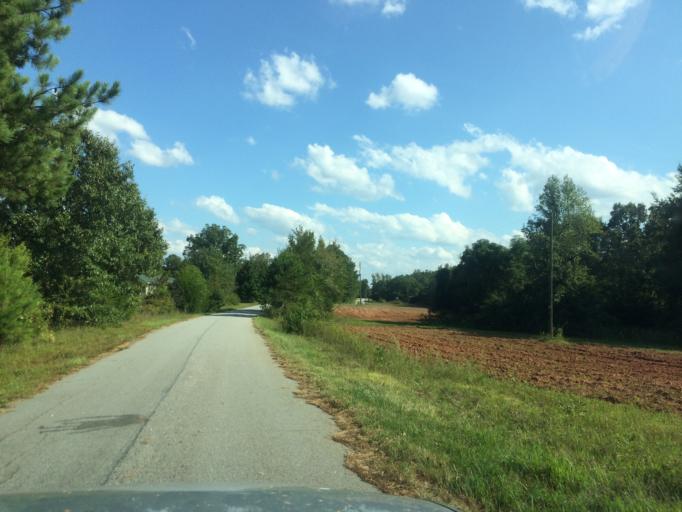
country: US
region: South Carolina
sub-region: Greenwood County
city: Ware Shoals
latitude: 34.4598
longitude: -82.1754
